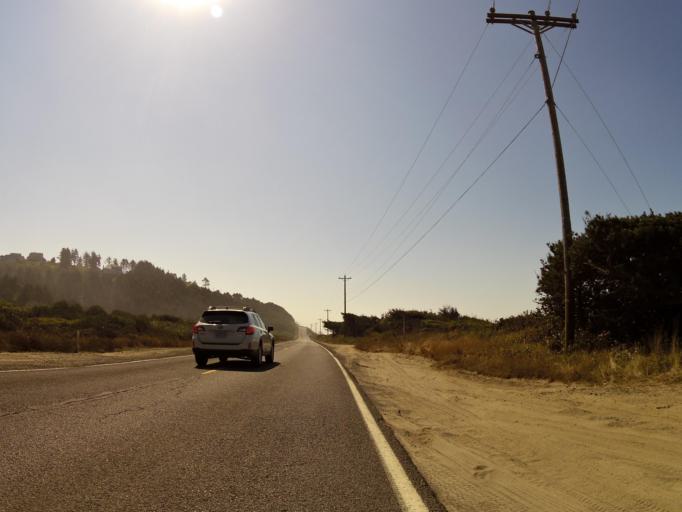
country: US
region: Oregon
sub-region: Tillamook County
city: Pacific City
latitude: 45.2454
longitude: -123.9676
